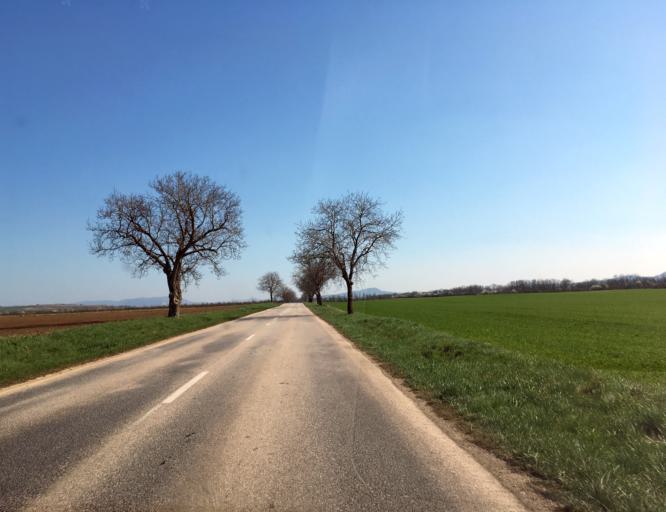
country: SK
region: Nitriansky
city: Svodin
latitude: 47.8402
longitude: 18.5360
